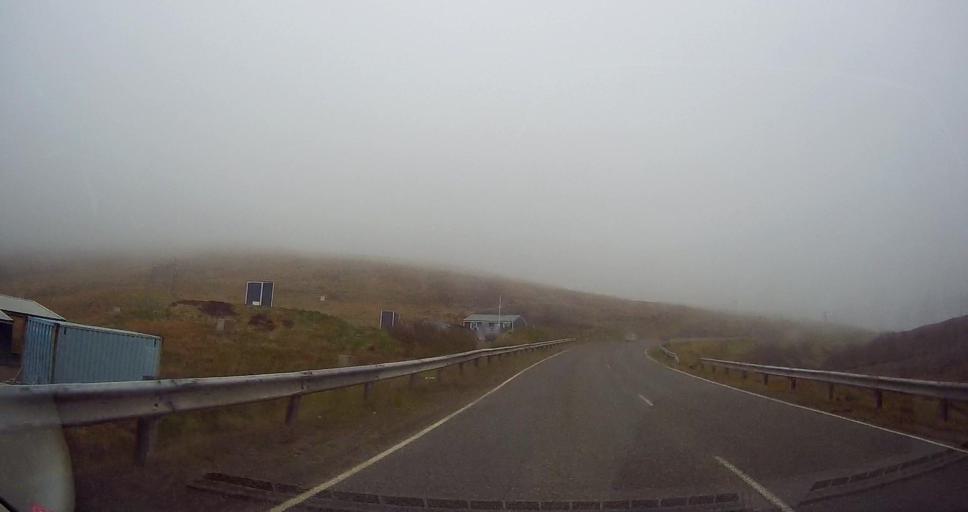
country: GB
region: Scotland
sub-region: Shetland Islands
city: Lerwick
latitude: 60.1409
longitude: -1.2404
